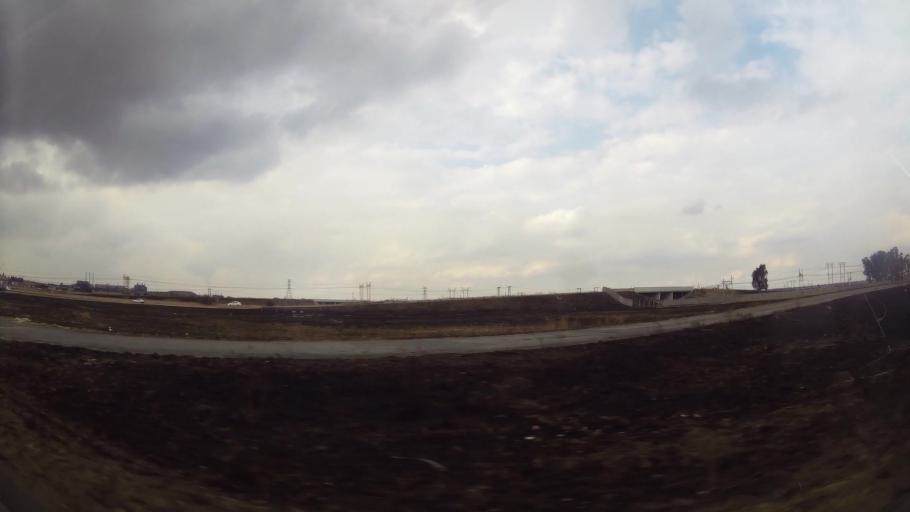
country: ZA
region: Orange Free State
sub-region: Fezile Dabi District Municipality
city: Sasolburg
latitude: -26.8418
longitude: 27.8718
